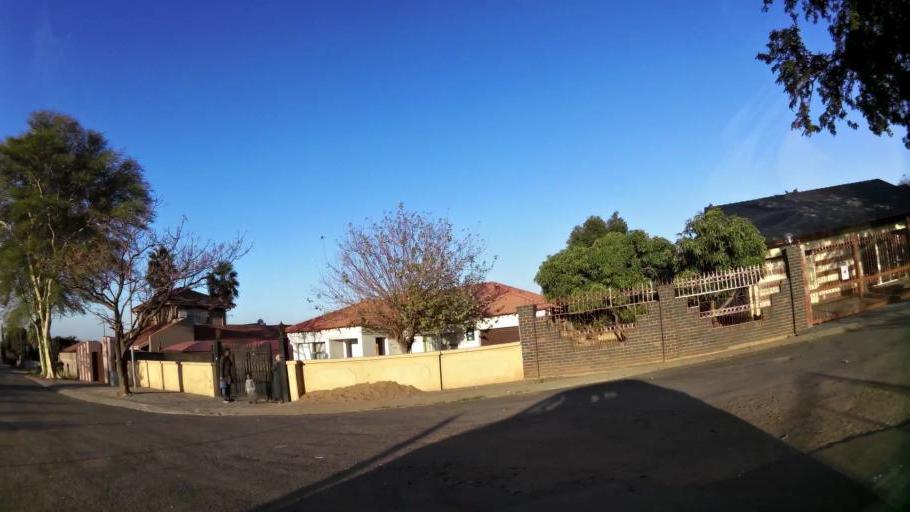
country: ZA
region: North-West
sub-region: Bojanala Platinum District Municipality
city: Rustenburg
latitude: -25.6400
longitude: 27.2028
